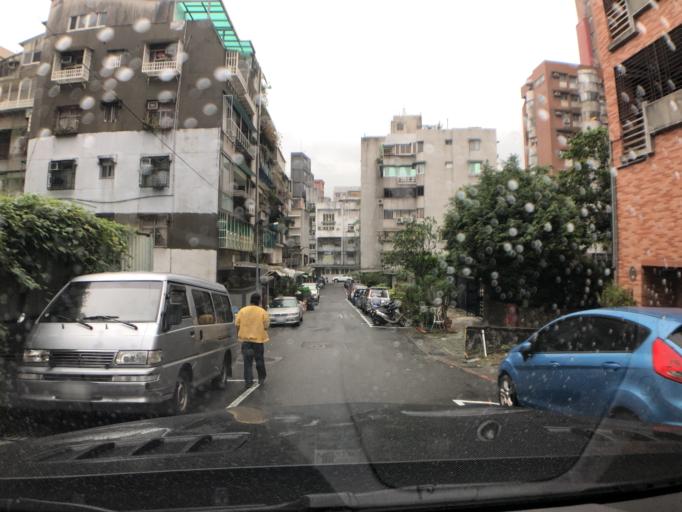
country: TW
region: Taipei
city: Taipei
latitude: 24.9858
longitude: 121.5619
